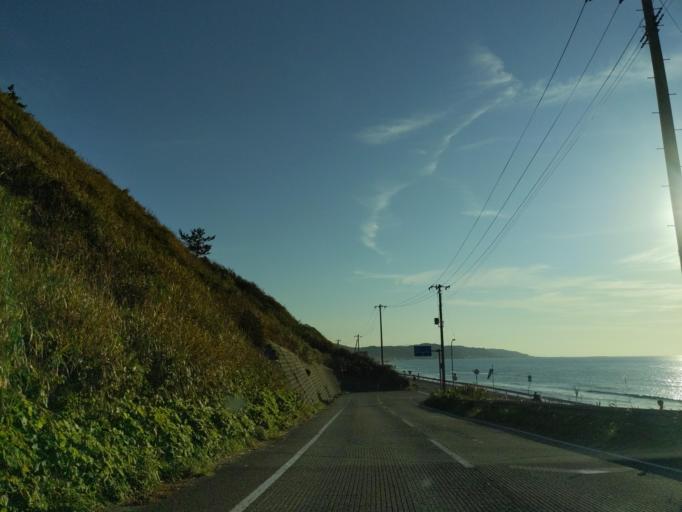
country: JP
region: Niigata
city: Nagaoka
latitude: 37.5766
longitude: 138.7264
